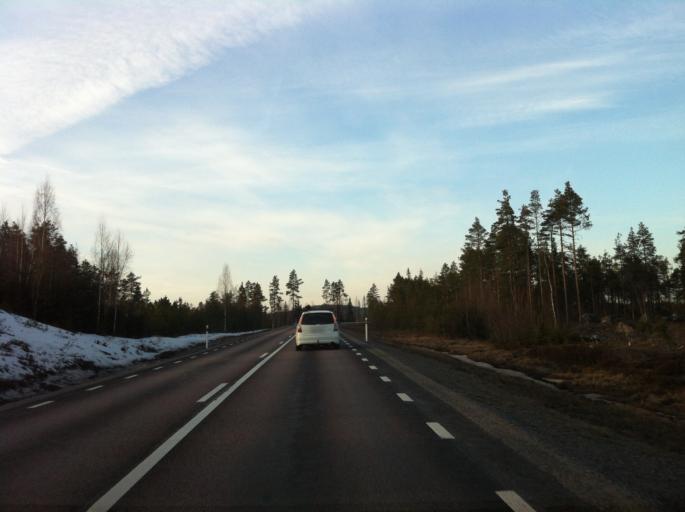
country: SE
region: Vaermland
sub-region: Filipstads Kommun
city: Lesjofors
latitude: 60.0597
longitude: 14.1392
